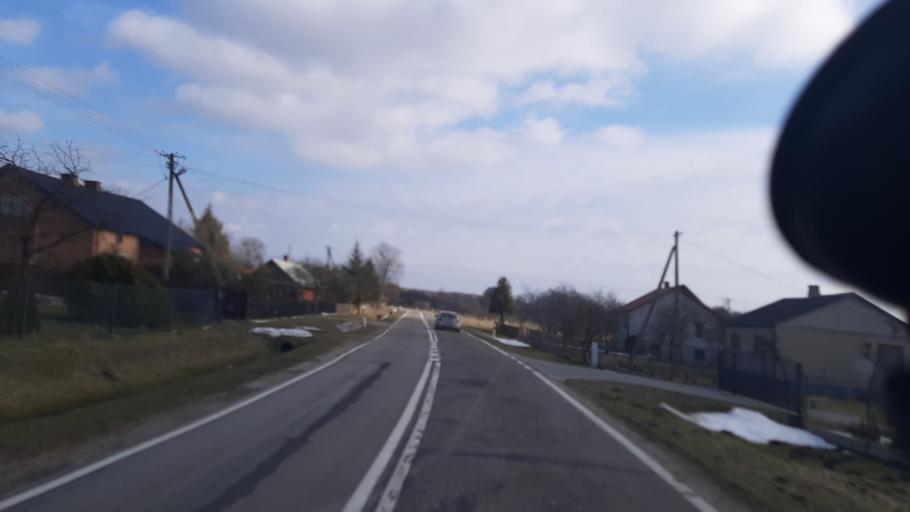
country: PL
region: Lublin Voivodeship
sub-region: Powiat parczewski
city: Sosnowica
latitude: 51.4983
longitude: 23.1624
